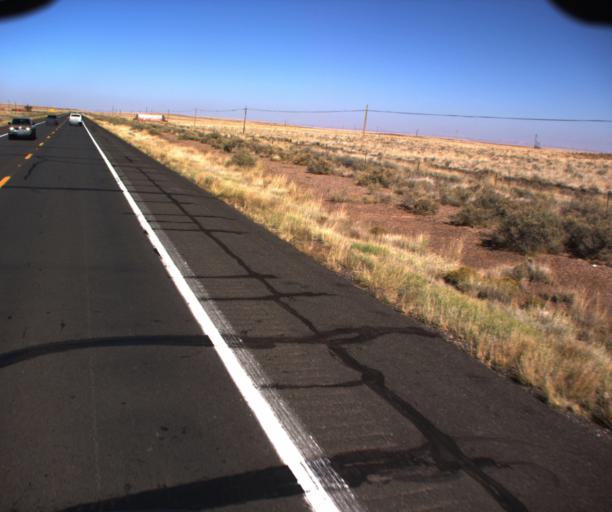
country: US
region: Arizona
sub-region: Coconino County
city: Flagstaff
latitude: 35.6791
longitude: -111.5078
